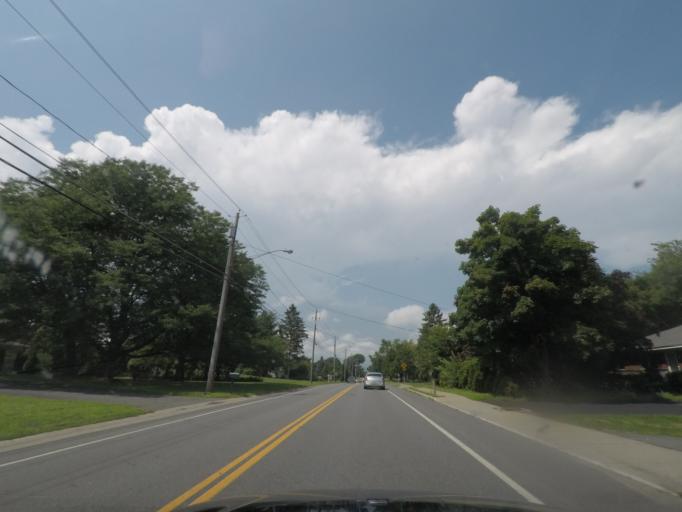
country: US
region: New York
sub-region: Albany County
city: Roessleville
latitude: 42.7135
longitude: -73.7831
